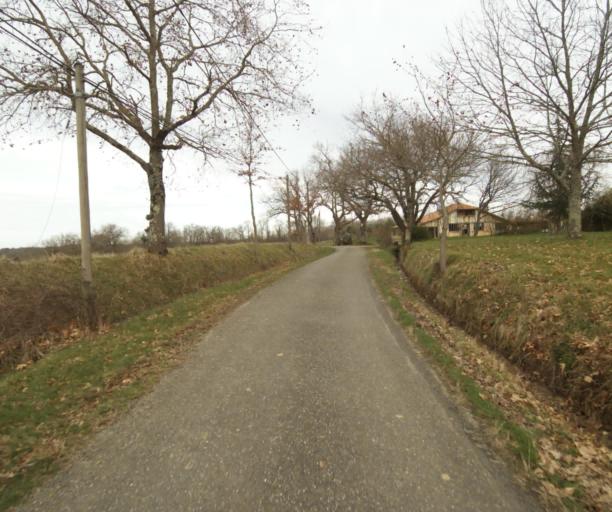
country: FR
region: Aquitaine
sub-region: Departement des Landes
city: Gabarret
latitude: 43.9245
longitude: 0.0334
